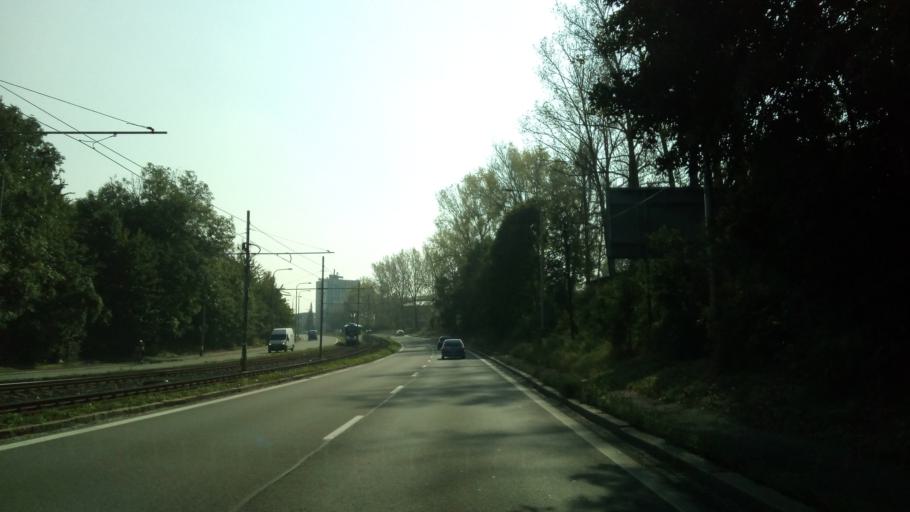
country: CZ
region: Moravskoslezsky
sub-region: Okres Ostrava-Mesto
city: Ostrava
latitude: 49.8181
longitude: 18.2368
